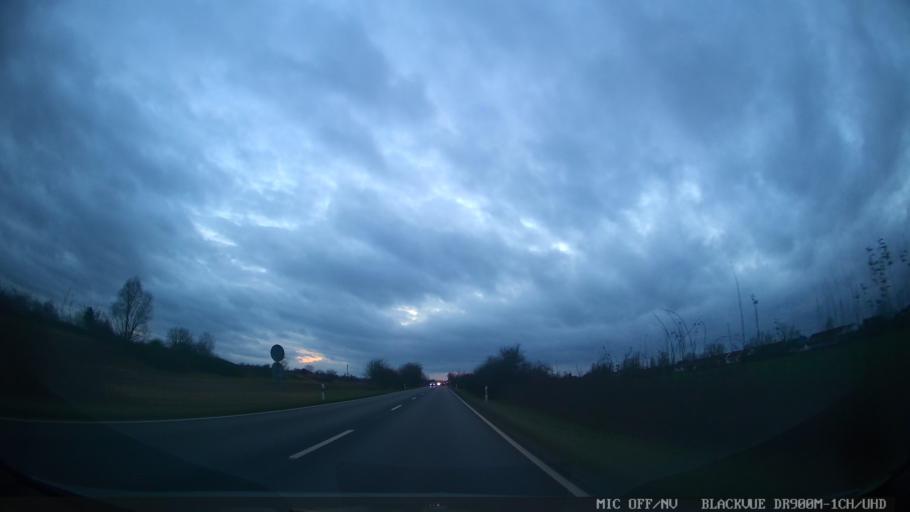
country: DE
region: Hesse
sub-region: Regierungsbezirk Darmstadt
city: Babenhausen
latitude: 49.9473
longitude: 8.9406
